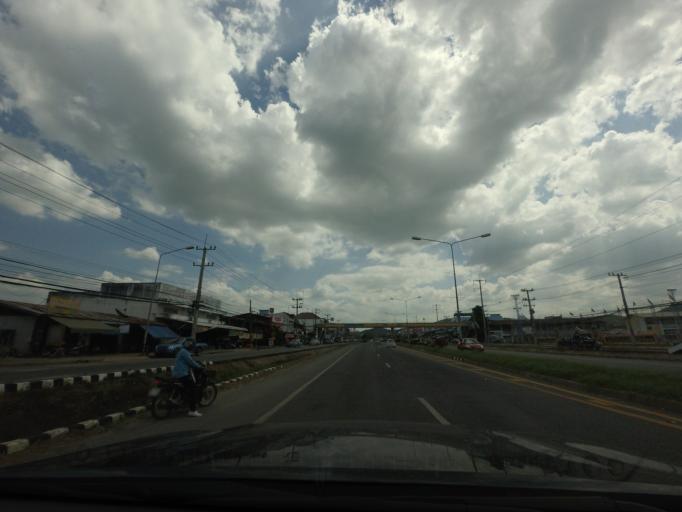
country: TH
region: Phetchabun
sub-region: Amphoe Bueng Sam Phan
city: Bueng Sam Phan
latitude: 15.7885
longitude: 101.0064
